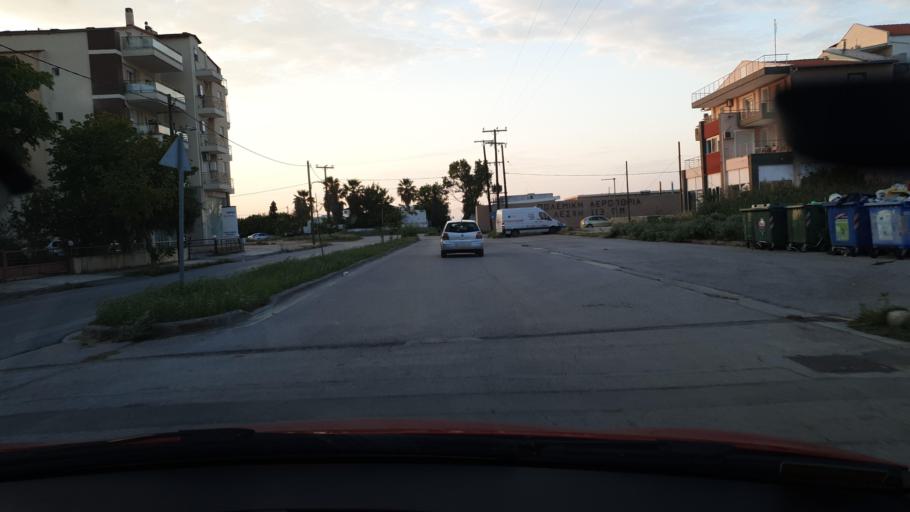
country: GR
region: Central Macedonia
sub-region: Nomos Thessalonikis
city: Peraia
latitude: 40.5104
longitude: 22.9355
